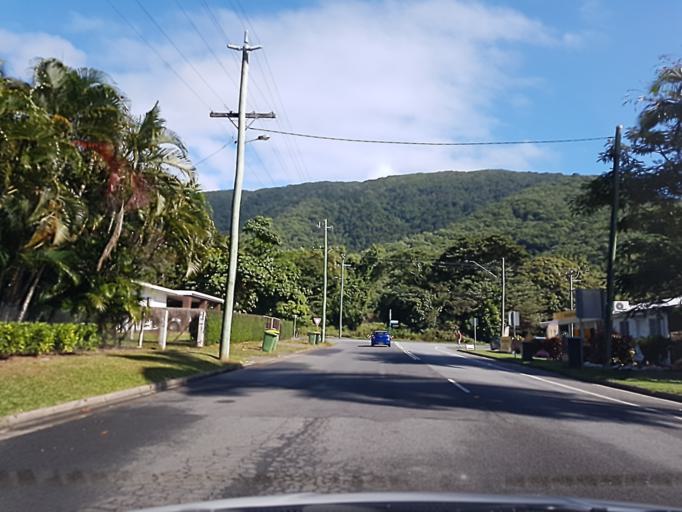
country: AU
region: Queensland
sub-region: Cairns
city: Palm Cove
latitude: -16.7481
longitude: 145.6636
